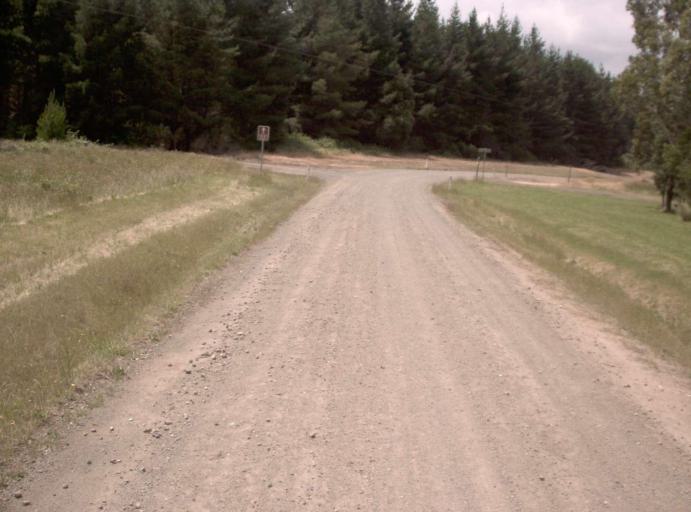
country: AU
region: Victoria
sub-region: Latrobe
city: Traralgon
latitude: -38.4013
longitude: 146.6479
